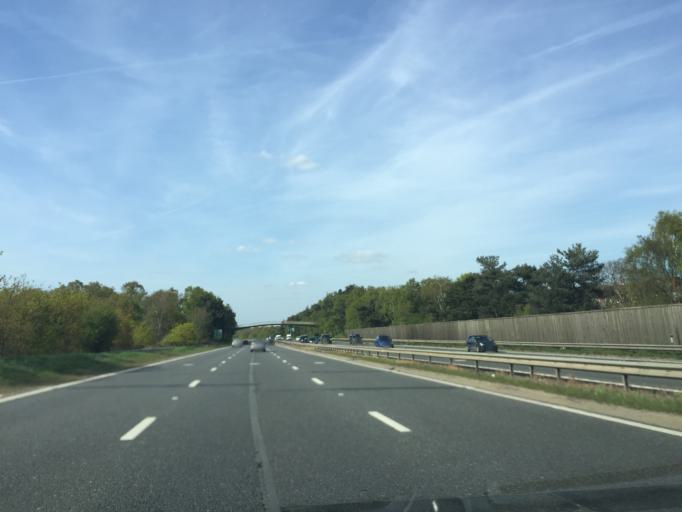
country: GB
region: England
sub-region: Kent
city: Swanley
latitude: 51.3977
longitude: 0.1584
